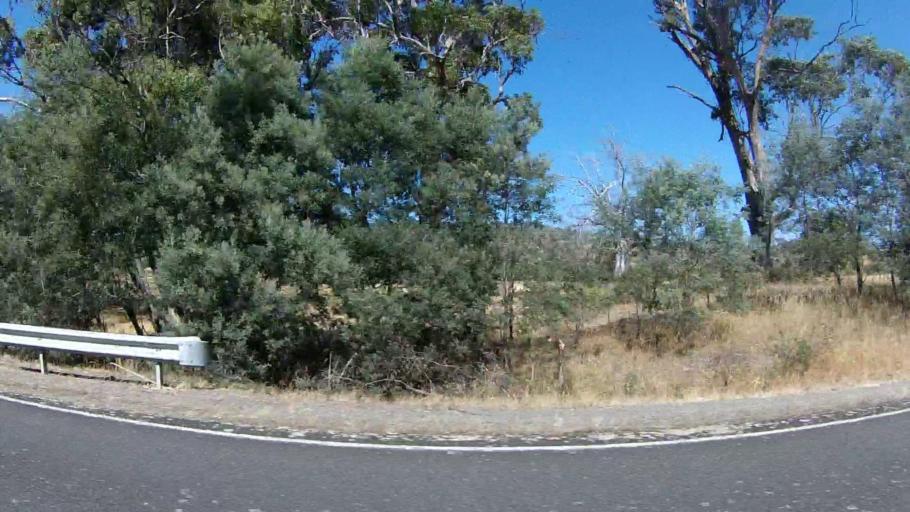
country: AU
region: Tasmania
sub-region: Sorell
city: Sorell
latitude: -42.5934
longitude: 147.7922
